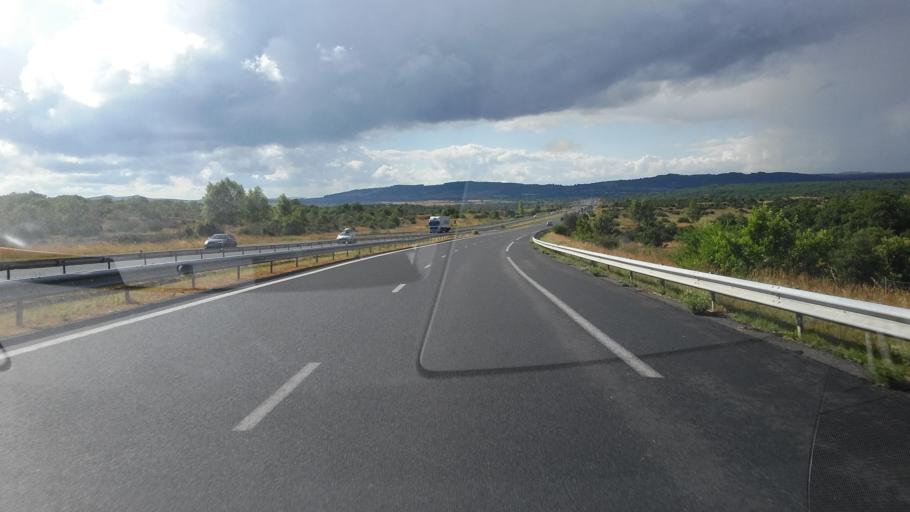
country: FR
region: Midi-Pyrenees
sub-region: Departement de l'Aveyron
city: La Cavalerie
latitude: 43.9238
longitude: 3.2405
